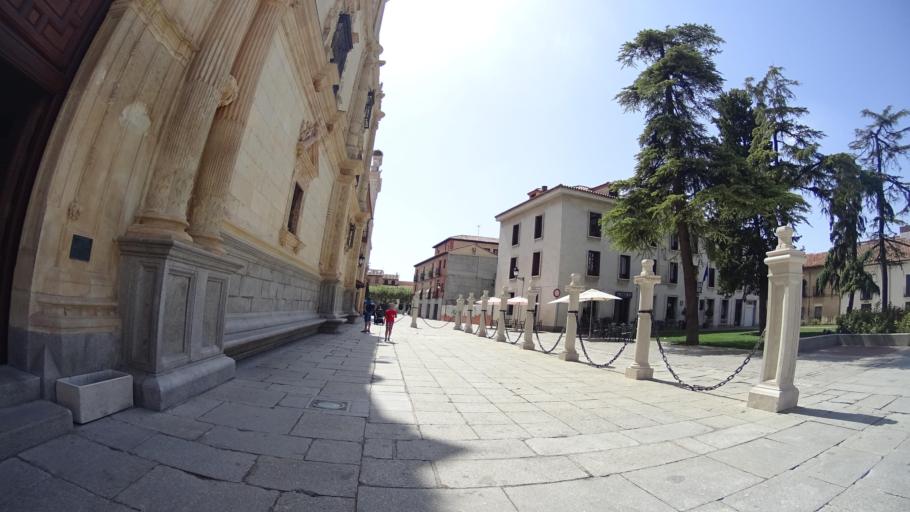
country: ES
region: Madrid
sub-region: Provincia de Madrid
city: Alcala de Henares
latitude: 40.4829
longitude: -3.3631
